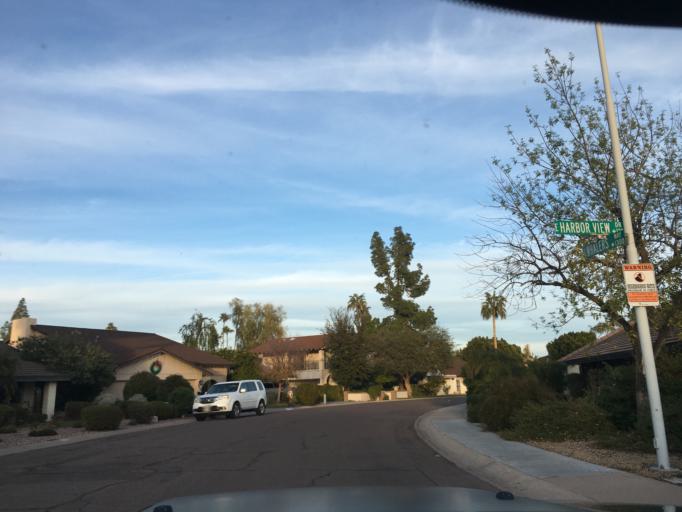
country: US
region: Arizona
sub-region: Maricopa County
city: Tempe
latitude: 33.3758
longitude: -111.9175
